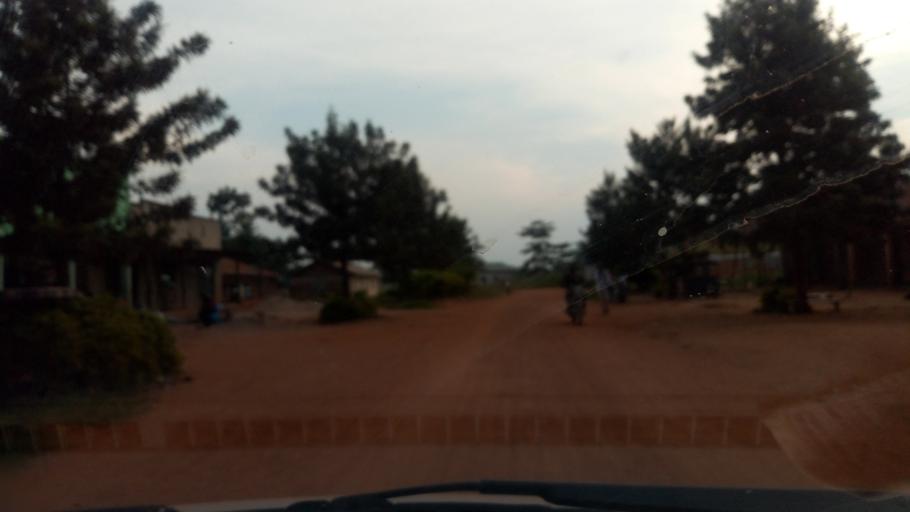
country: UG
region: Western Region
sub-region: Kiryandongo District
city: Kiryandongo
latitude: 1.8096
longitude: 32.0065
